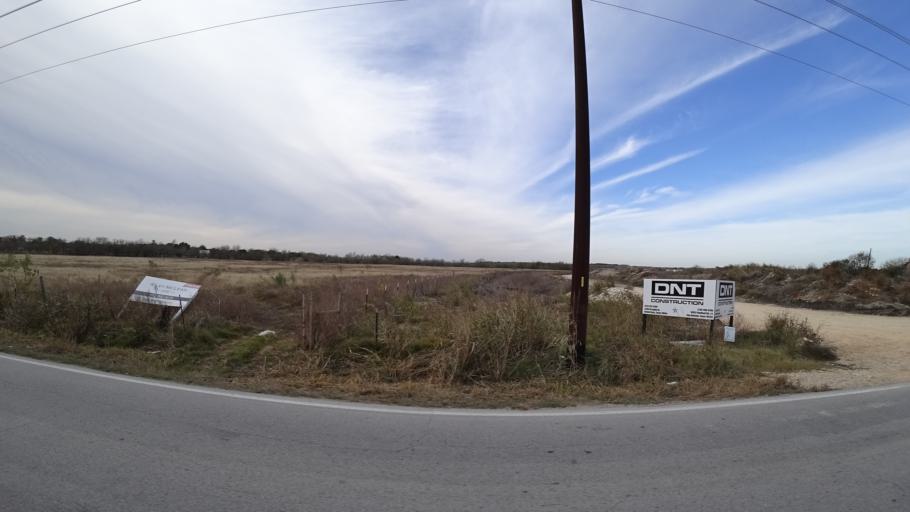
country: US
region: Texas
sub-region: Travis County
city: Onion Creek
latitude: 30.1449
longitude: -97.7299
